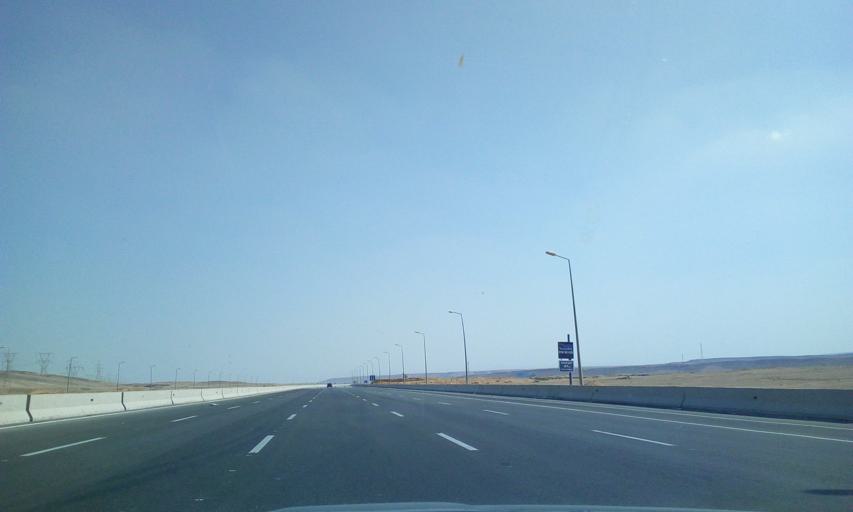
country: EG
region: As Suways
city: Ain Sukhna
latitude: 29.8174
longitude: 31.8936
